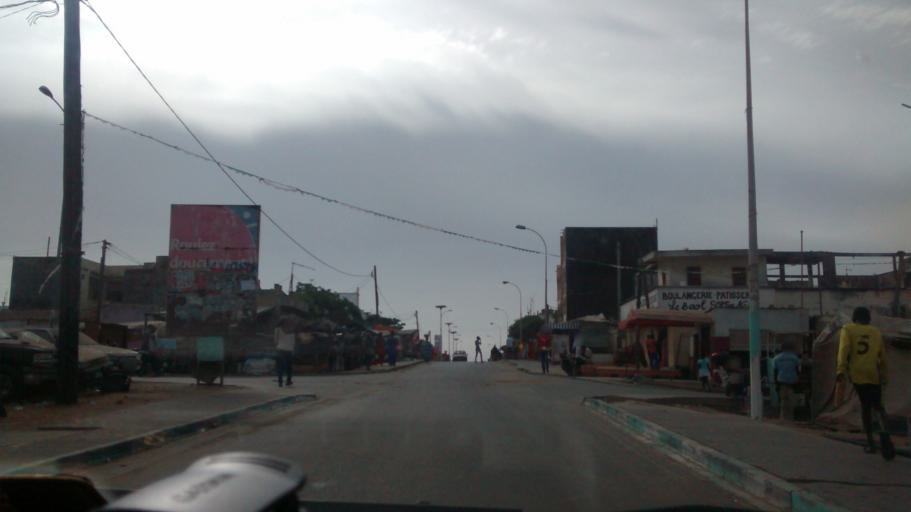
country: SN
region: Dakar
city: Pikine
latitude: 14.7827
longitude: -17.3820
